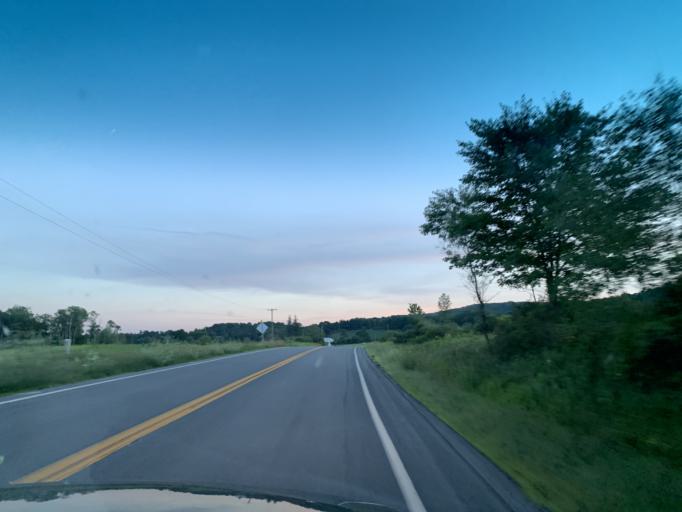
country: US
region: New York
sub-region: Chenango County
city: New Berlin
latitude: 42.7233
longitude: -75.3047
